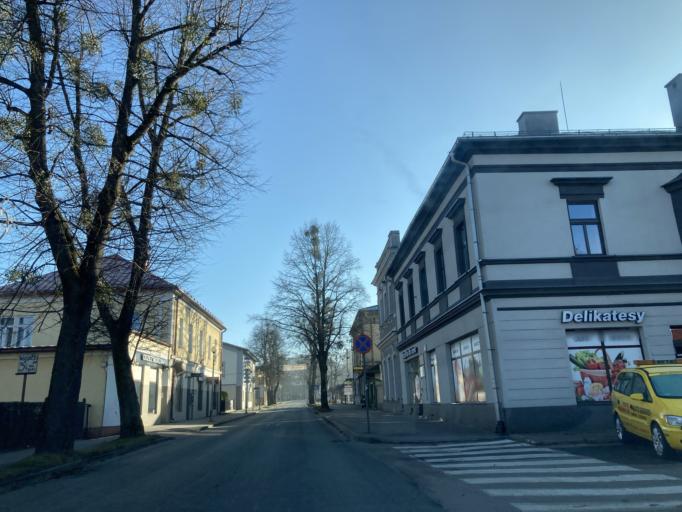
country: PL
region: Silesian Voivodeship
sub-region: Powiat cieszynski
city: Ustron
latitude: 49.7184
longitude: 18.8135
